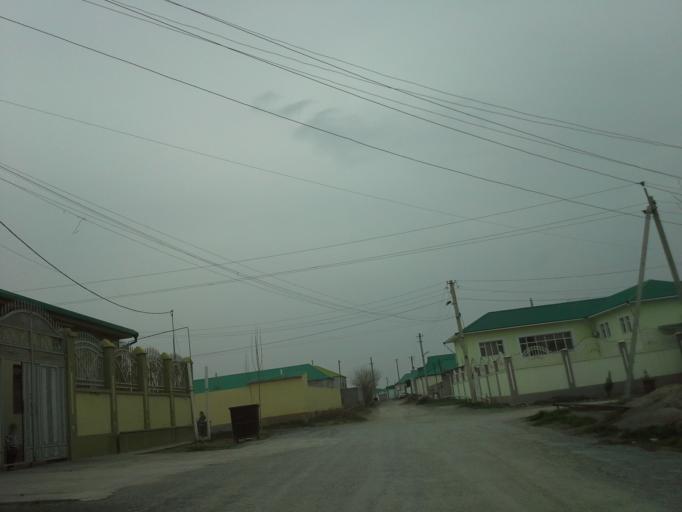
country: TM
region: Ahal
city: Abadan
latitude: 37.9785
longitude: 58.2237
